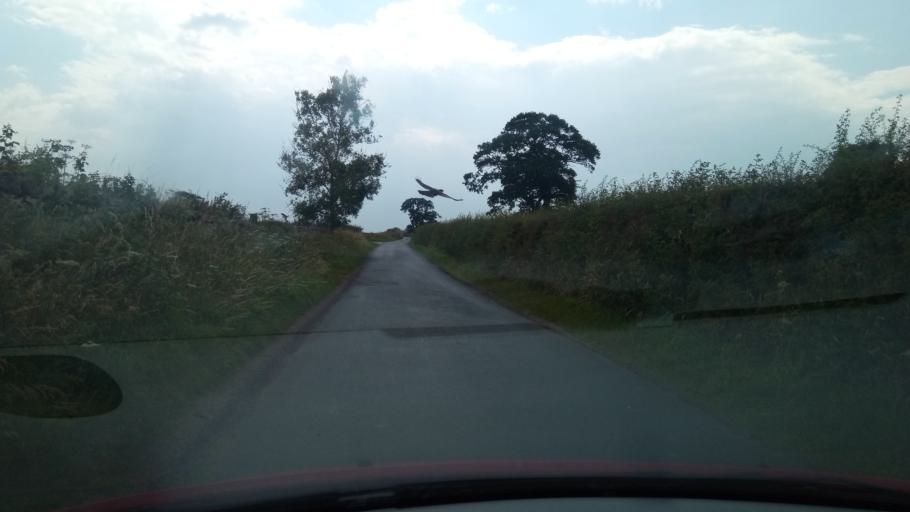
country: GB
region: Scotland
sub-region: The Scottish Borders
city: Kelso
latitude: 55.5766
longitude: -2.4757
